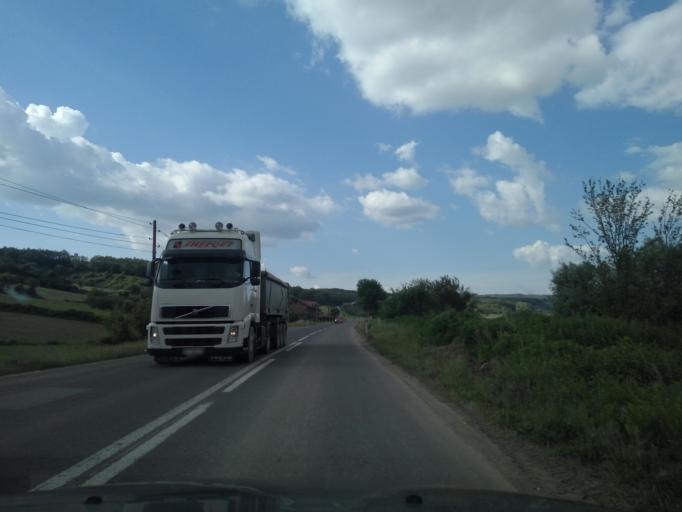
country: XK
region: Pec
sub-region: Komuna e Pejes
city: Kosuriq
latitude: 42.4743
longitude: 20.5032
